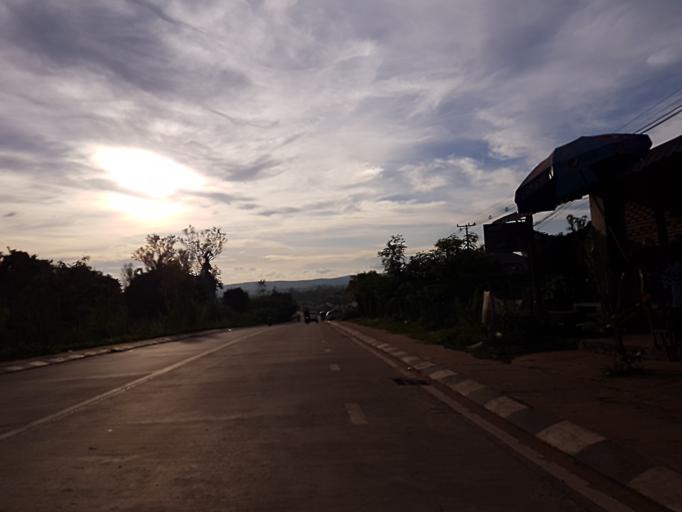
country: TH
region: Nong Khai
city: Si Chiang Mai
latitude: 18.0203
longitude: 102.5138
